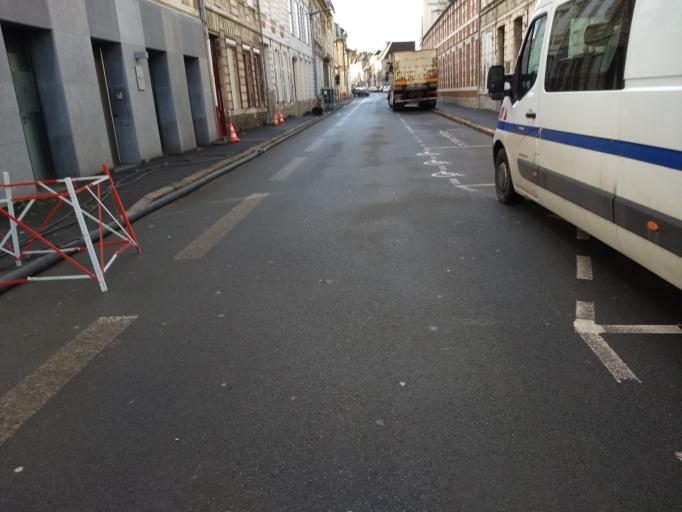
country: FR
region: Nord-Pas-de-Calais
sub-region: Departement du Pas-de-Calais
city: Arras
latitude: 50.2918
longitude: 2.7671
